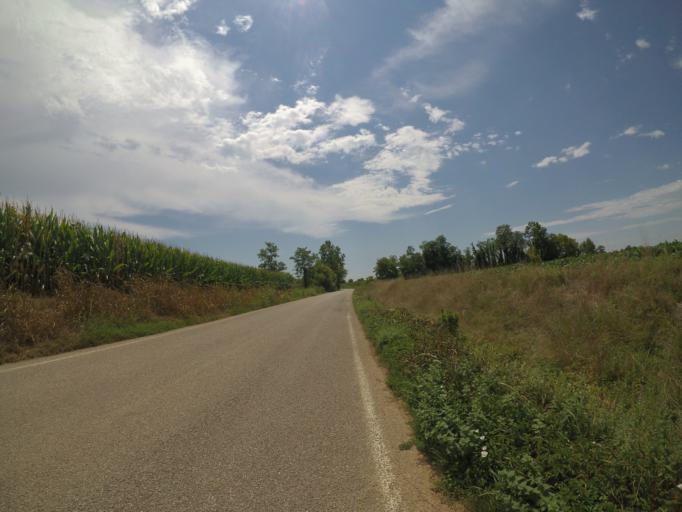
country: IT
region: Friuli Venezia Giulia
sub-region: Provincia di Udine
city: Talmassons
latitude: 45.9471
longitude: 13.0956
